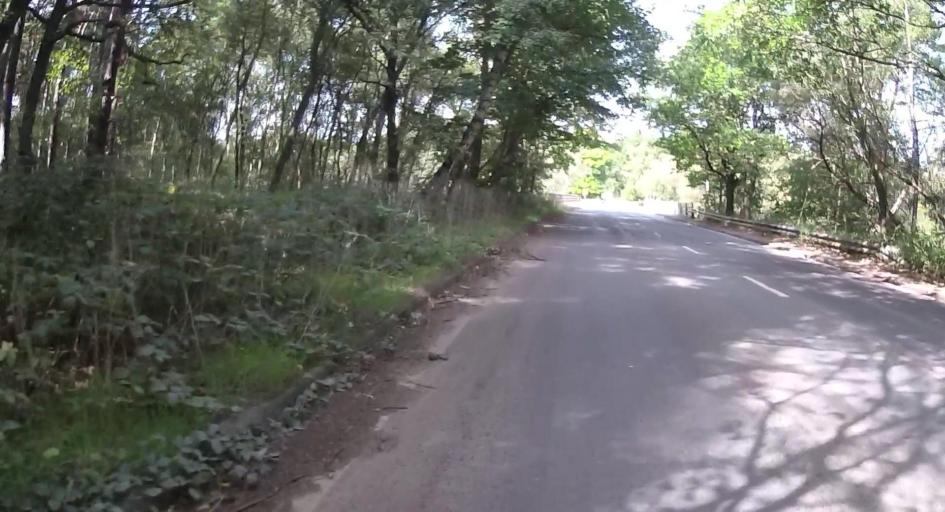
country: GB
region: England
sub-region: Surrey
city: Virginia Water
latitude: 51.3861
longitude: -0.5771
